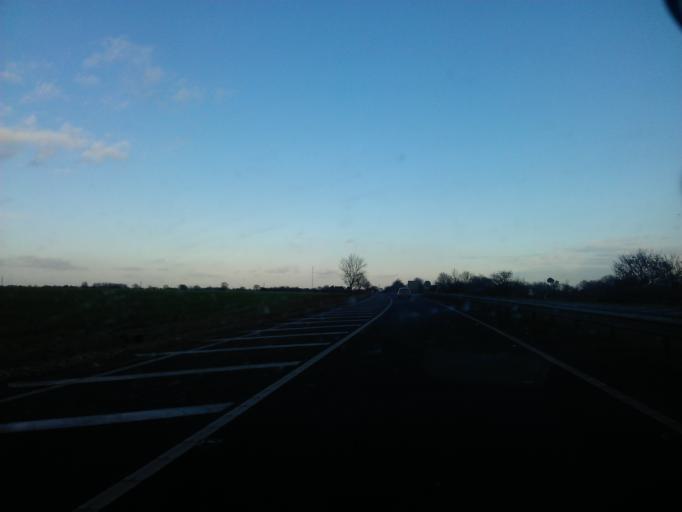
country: GB
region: England
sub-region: Essex
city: Great Bentley
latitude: 51.8887
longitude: 1.0616
